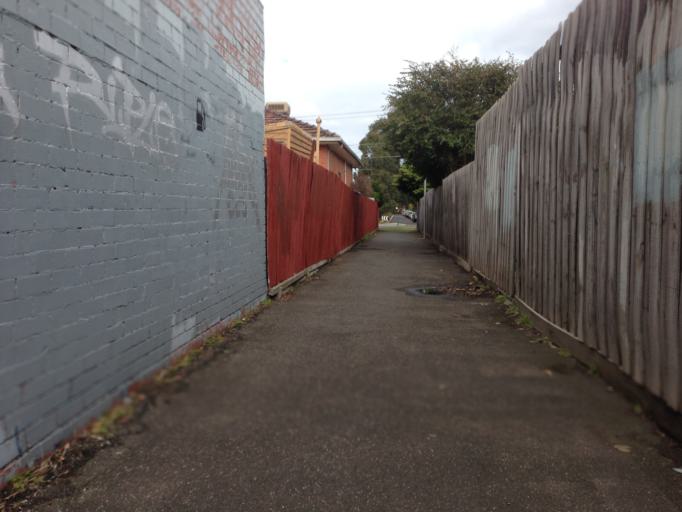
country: AU
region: Victoria
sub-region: Darebin
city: Fairfield
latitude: -37.7796
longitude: 145.0089
